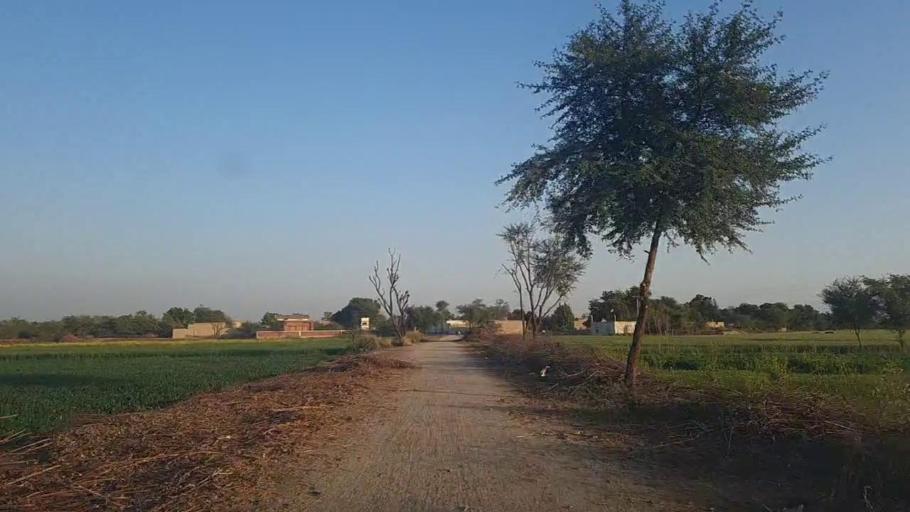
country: PK
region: Sindh
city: Jam Sahib
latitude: 26.3223
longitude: 68.7004
